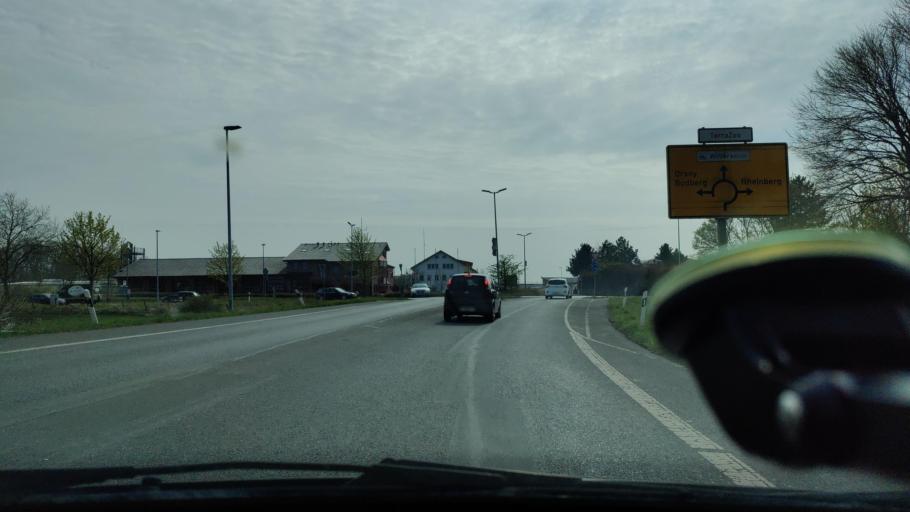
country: DE
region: North Rhine-Westphalia
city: Rheinberg
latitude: 51.5407
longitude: 6.6134
